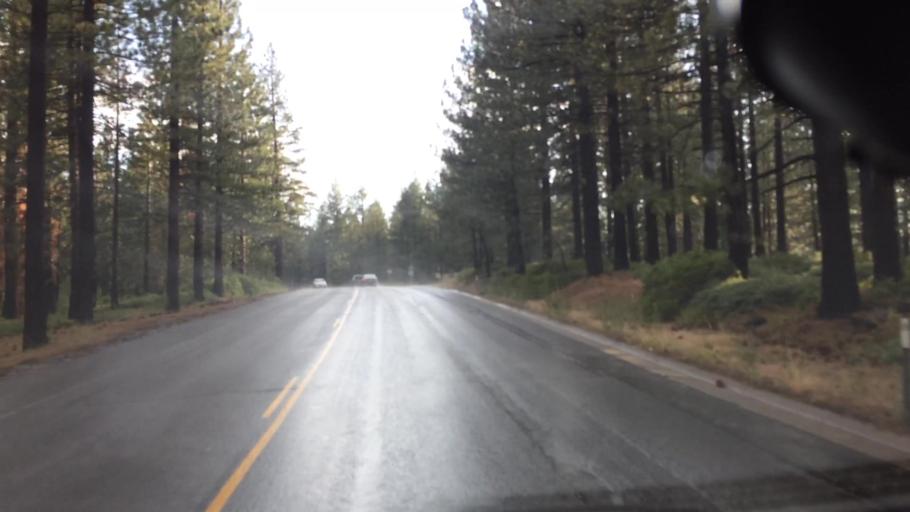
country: US
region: California
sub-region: El Dorado County
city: South Lake Tahoe
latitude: 38.8854
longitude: -119.9841
